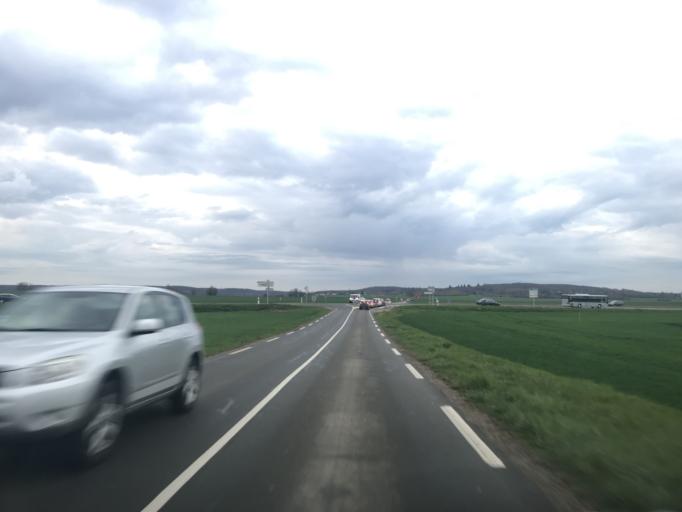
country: FR
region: Ile-de-France
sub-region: Departement des Yvelines
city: Villiers-Saint-Frederic
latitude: 48.8057
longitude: 1.8673
